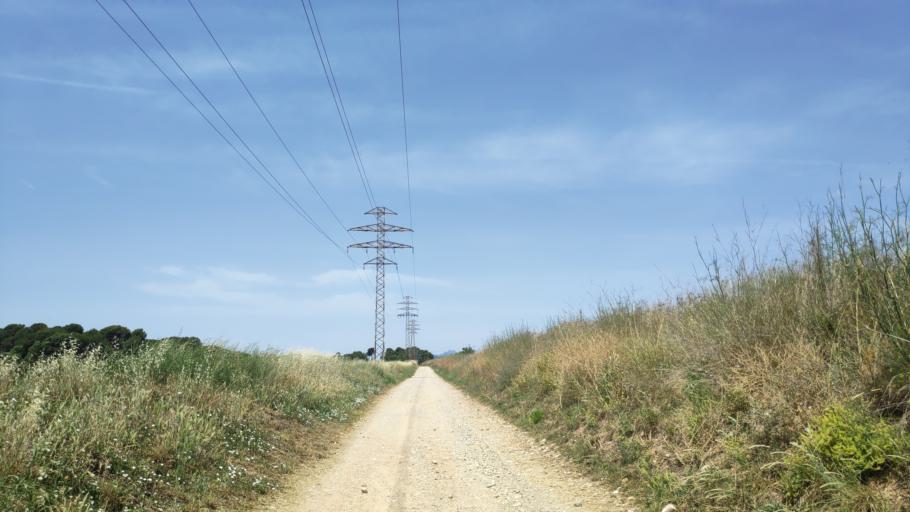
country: ES
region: Catalonia
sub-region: Provincia de Barcelona
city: Sant Quirze del Valles
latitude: 41.5651
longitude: 2.0601
